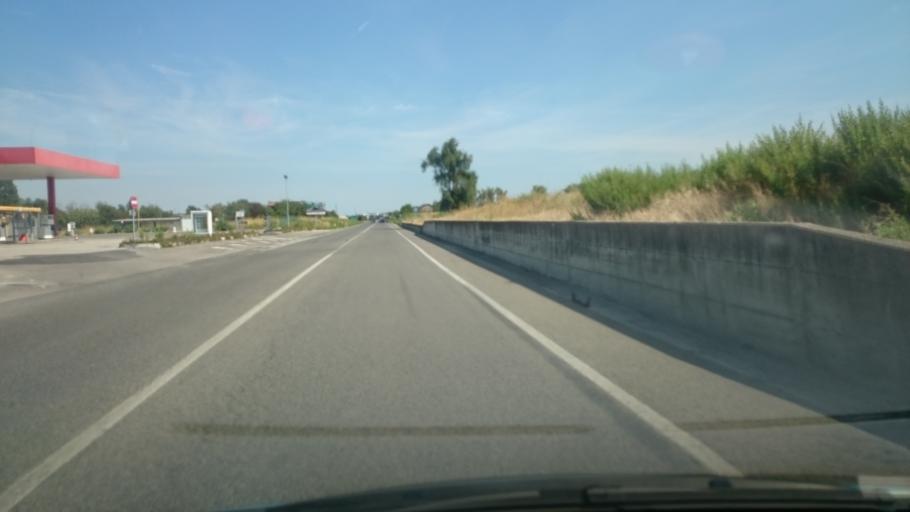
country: IT
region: Emilia-Romagna
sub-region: Provincia di Reggio Emilia
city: Casalgrande
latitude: 44.5908
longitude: 10.7158
